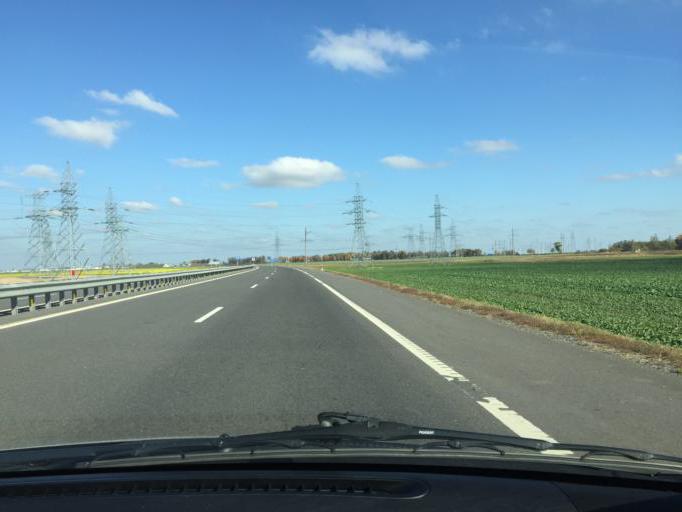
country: BY
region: Minsk
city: Slutsk
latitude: 53.0539
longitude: 27.5379
